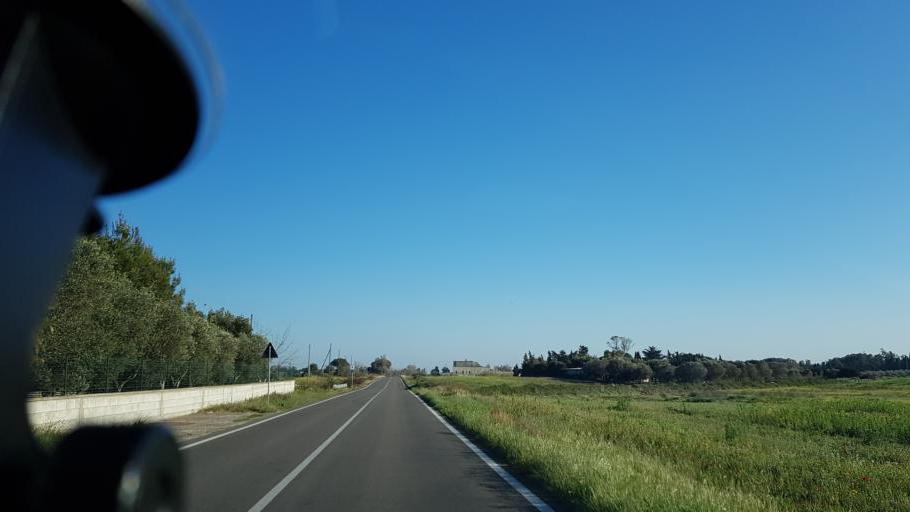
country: IT
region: Apulia
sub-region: Provincia di Lecce
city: Merine
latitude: 40.4162
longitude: 18.2518
